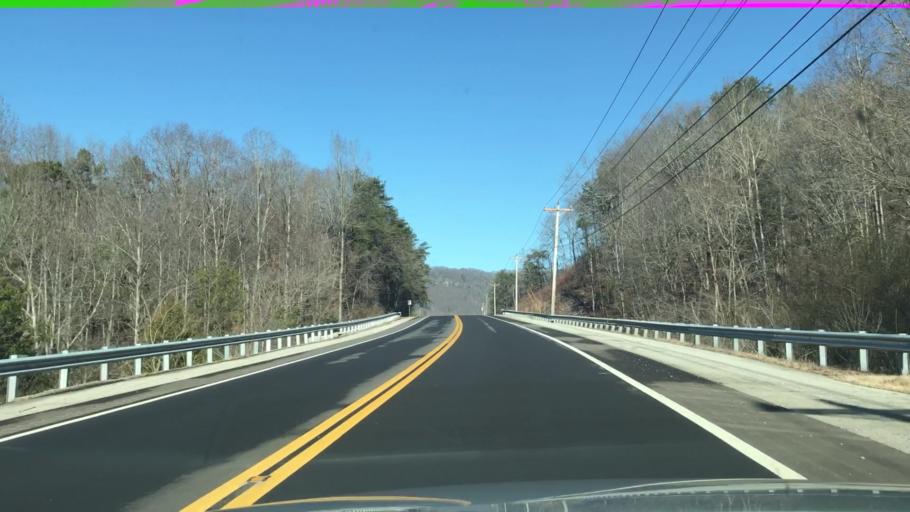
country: US
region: Tennessee
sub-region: Roane County
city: Midtown
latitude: 35.8898
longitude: -84.6174
